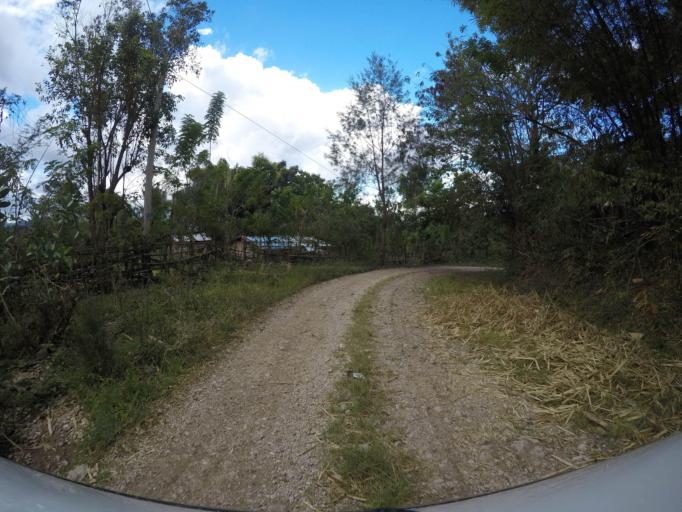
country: TL
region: Baucau
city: Venilale
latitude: -8.6823
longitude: 126.6494
